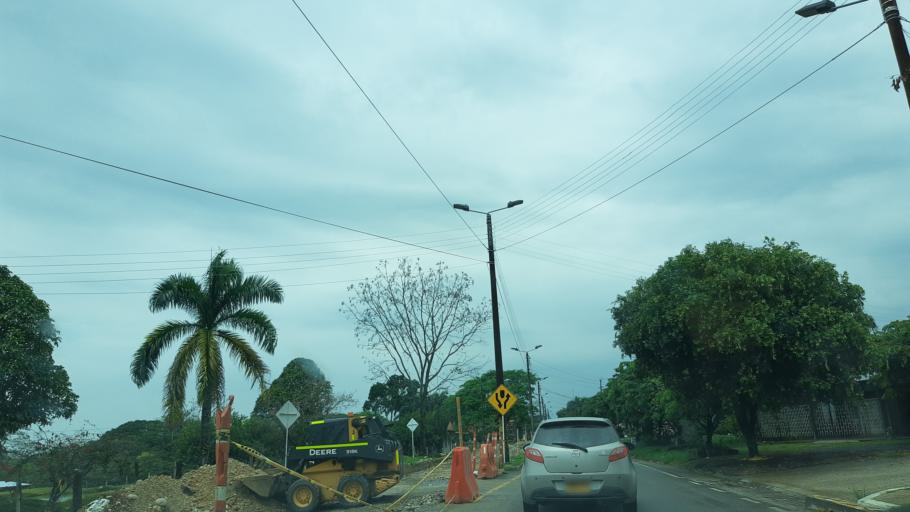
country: CO
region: Casanare
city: Monterrey
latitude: 4.8386
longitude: -72.9552
